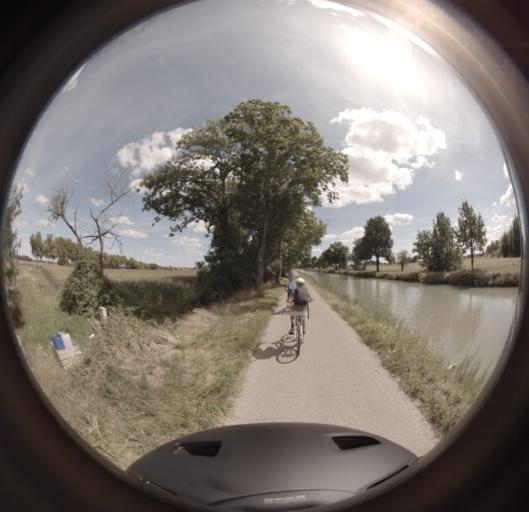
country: FR
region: Midi-Pyrenees
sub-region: Departement du Tarn-et-Garonne
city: Saint-Porquier
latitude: 44.0289
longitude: 1.1446
